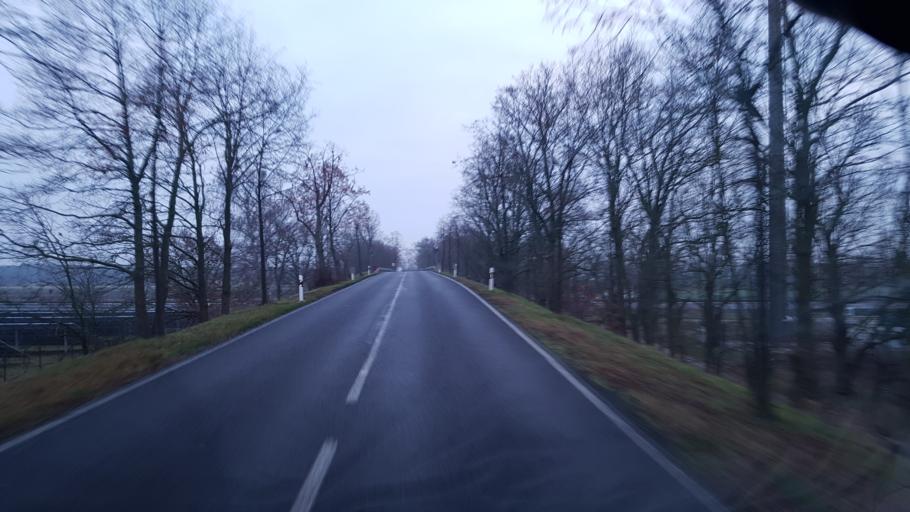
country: DE
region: Brandenburg
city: Ludwigsfelde
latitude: 52.3017
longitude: 13.1639
